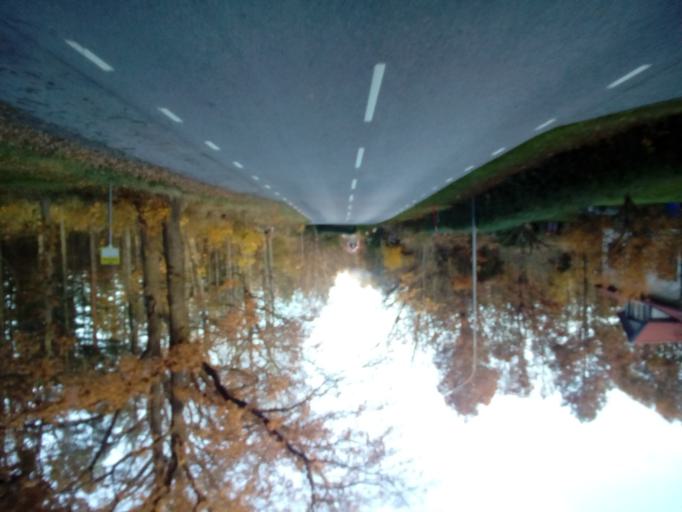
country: SE
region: Kalmar
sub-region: Vimmerby Kommun
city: Vimmerby
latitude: 57.7245
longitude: 16.0691
